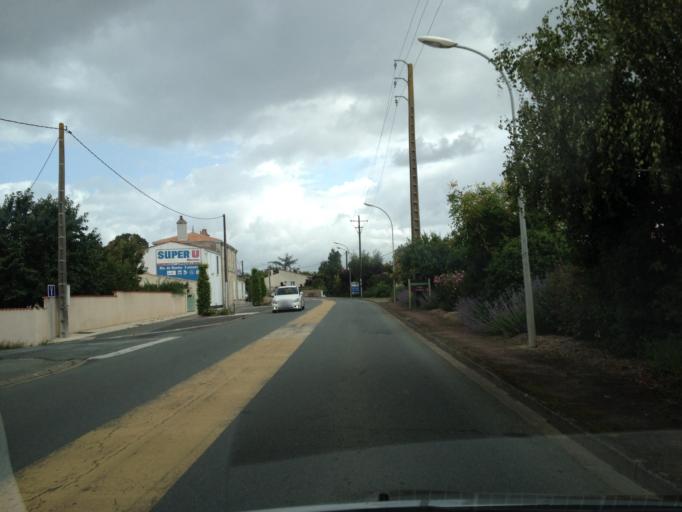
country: FR
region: Poitou-Charentes
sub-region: Departement de la Charente-Maritime
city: Marans
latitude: 46.3029
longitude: -0.9898
